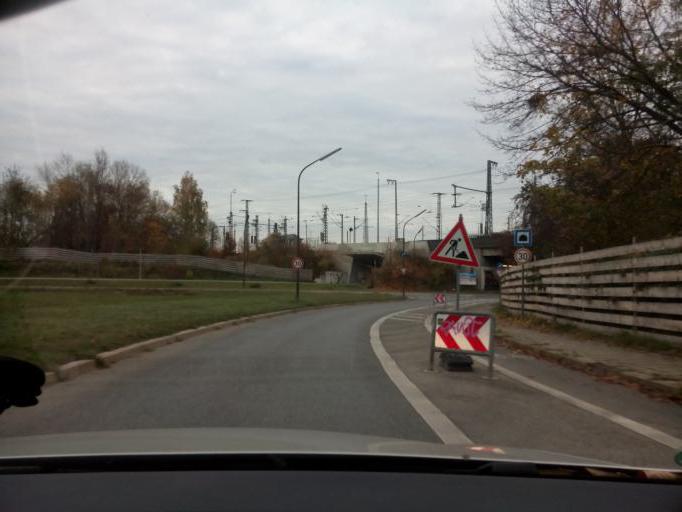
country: DE
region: Bavaria
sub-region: Upper Bavaria
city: Bogenhausen
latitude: 48.1361
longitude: 11.6327
